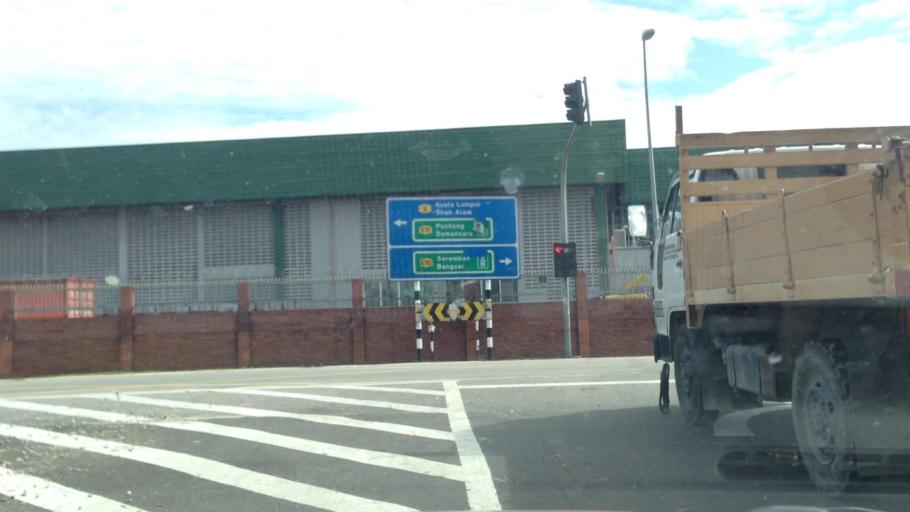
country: MY
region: Selangor
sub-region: Petaling
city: Petaling Jaya
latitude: 3.0820
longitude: 101.6202
